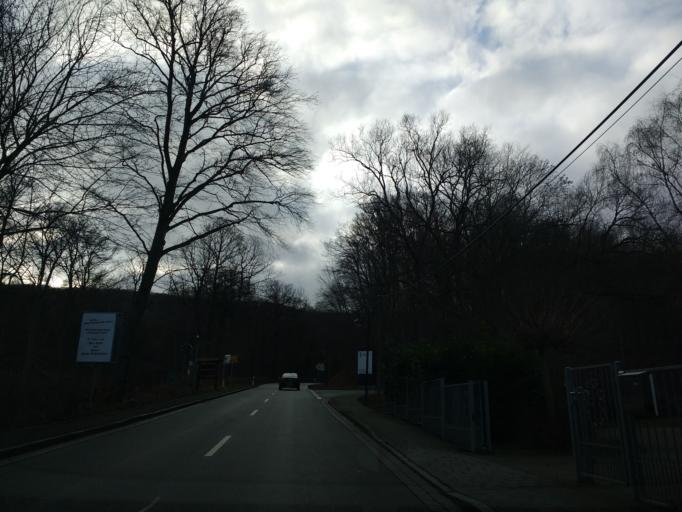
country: DE
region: Saxony-Anhalt
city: Bad Suderode
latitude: 51.7244
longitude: 11.1151
